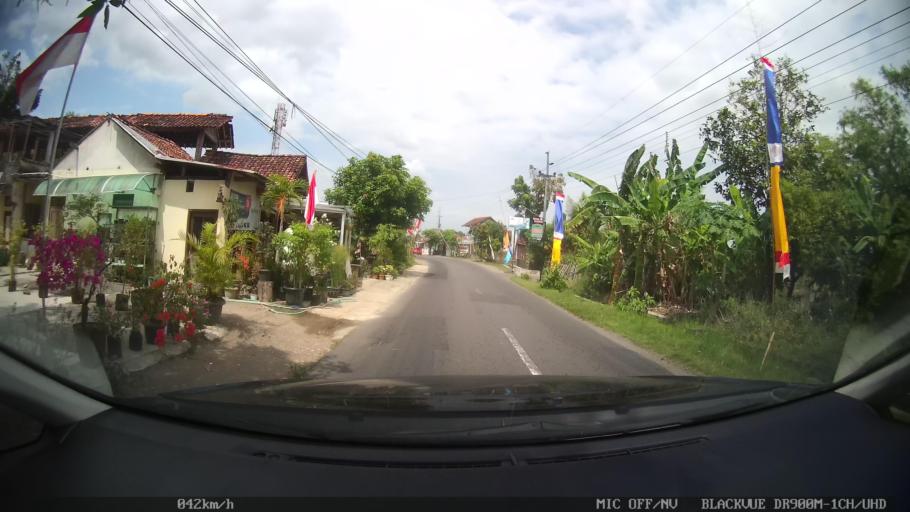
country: ID
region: Daerah Istimewa Yogyakarta
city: Depok
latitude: -7.8032
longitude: 110.4530
